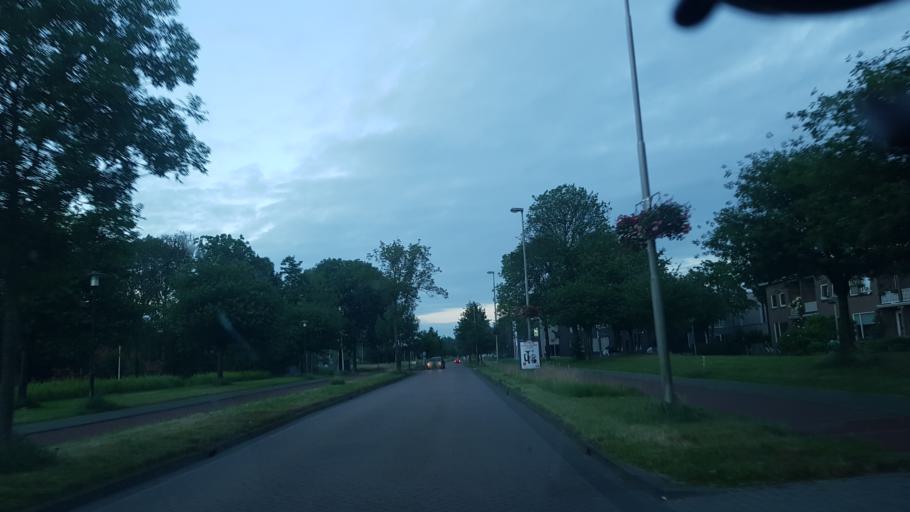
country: NL
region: Friesland
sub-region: Gemeente Leeuwarden
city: Leeuwarden
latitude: 53.2090
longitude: 5.8225
